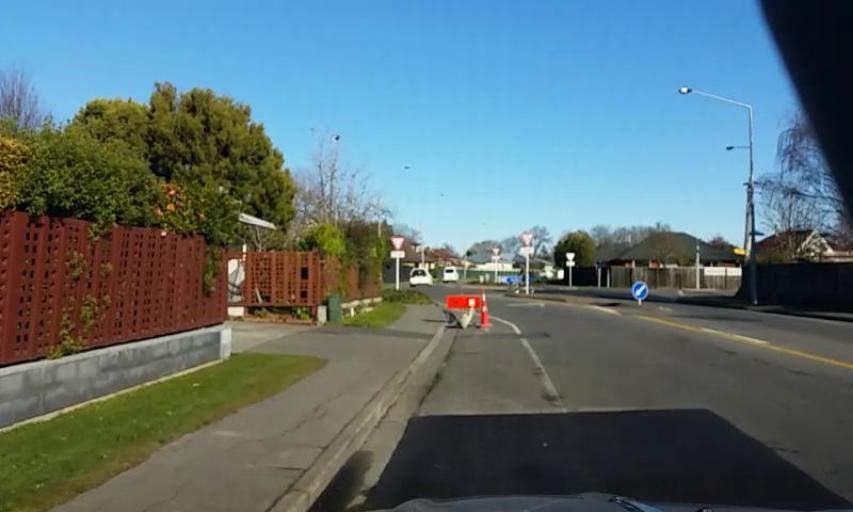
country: NZ
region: Canterbury
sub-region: Christchurch City
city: Christchurch
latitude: -43.5083
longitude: 172.6429
